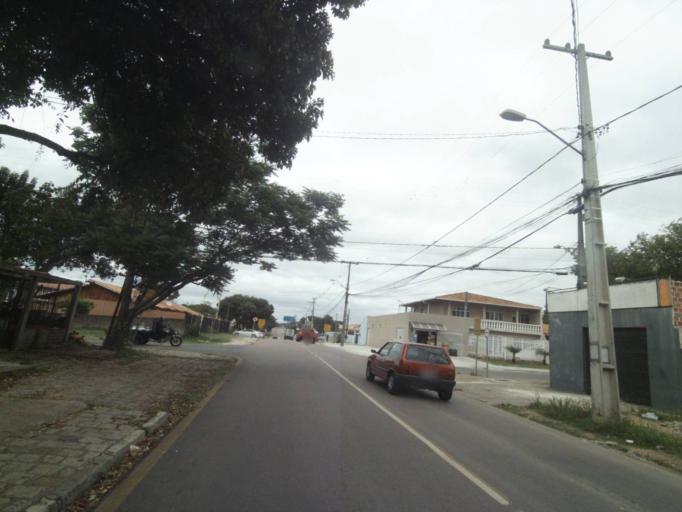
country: BR
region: Parana
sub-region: Sao Jose Dos Pinhais
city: Sao Jose dos Pinhais
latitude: -25.5510
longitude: -49.2736
